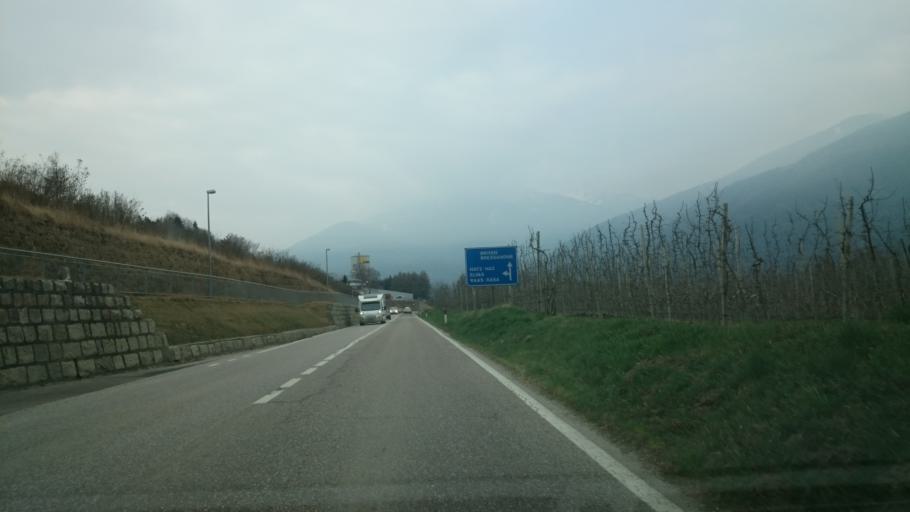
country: IT
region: Trentino-Alto Adige
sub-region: Bolzano
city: Naz-Sciaves - Natz-Schabs
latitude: 46.7684
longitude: 11.6637
